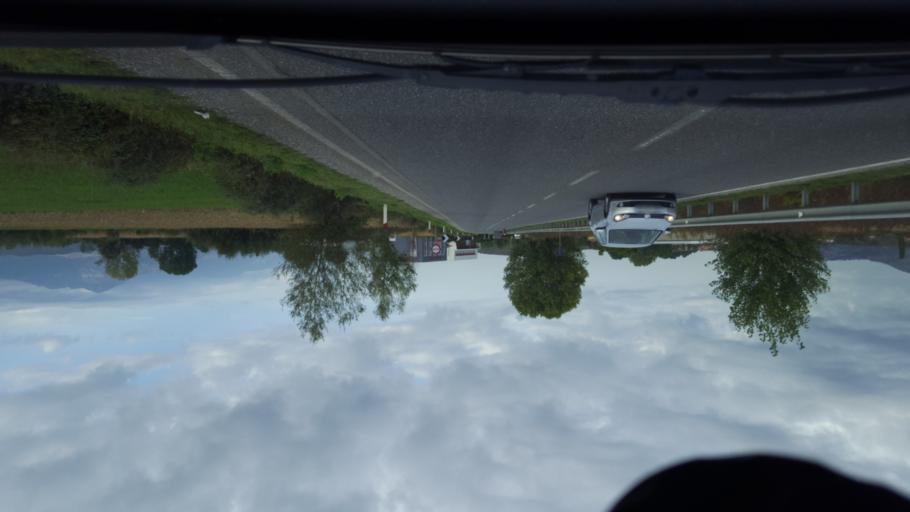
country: AL
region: Shkoder
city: Vukatane
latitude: 42.0048
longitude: 19.5227
